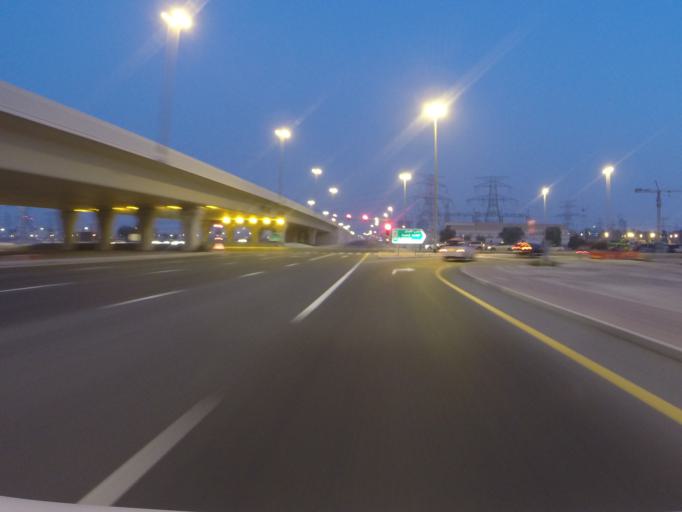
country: AE
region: Dubai
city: Dubai
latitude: 25.0686
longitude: 55.1920
